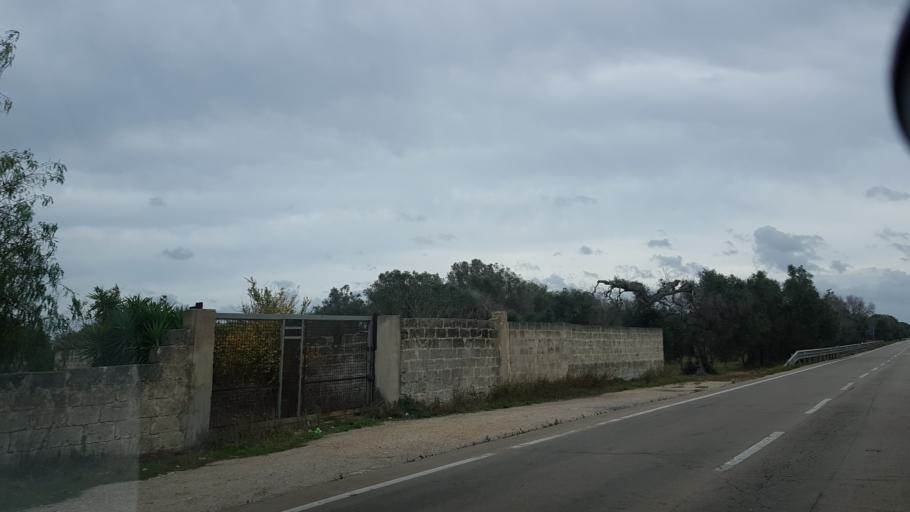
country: IT
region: Apulia
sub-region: Provincia di Lecce
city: Guagnano
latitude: 40.3989
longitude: 17.9283
